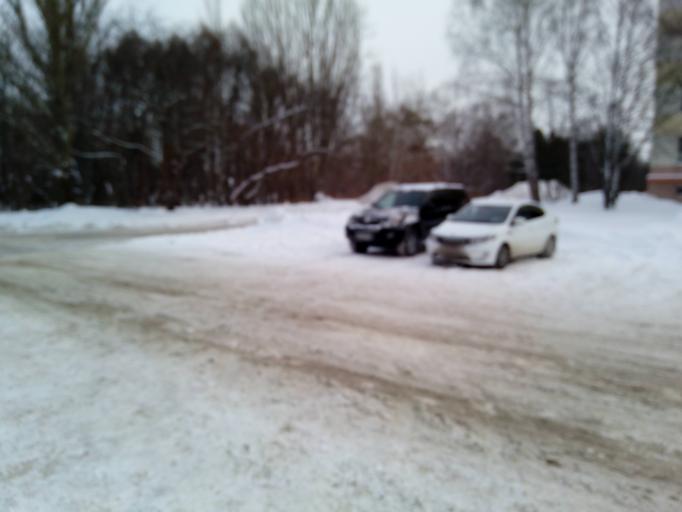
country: RU
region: Novosibirsk
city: Akademgorodok
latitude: 54.8525
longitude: 83.1019
